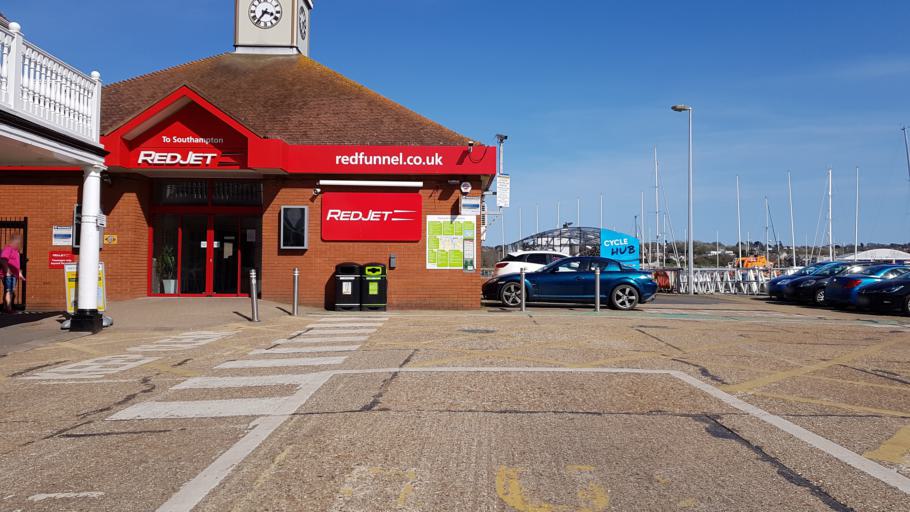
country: GB
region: England
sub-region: Isle of Wight
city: Cowes
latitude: 50.7627
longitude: -1.2972
